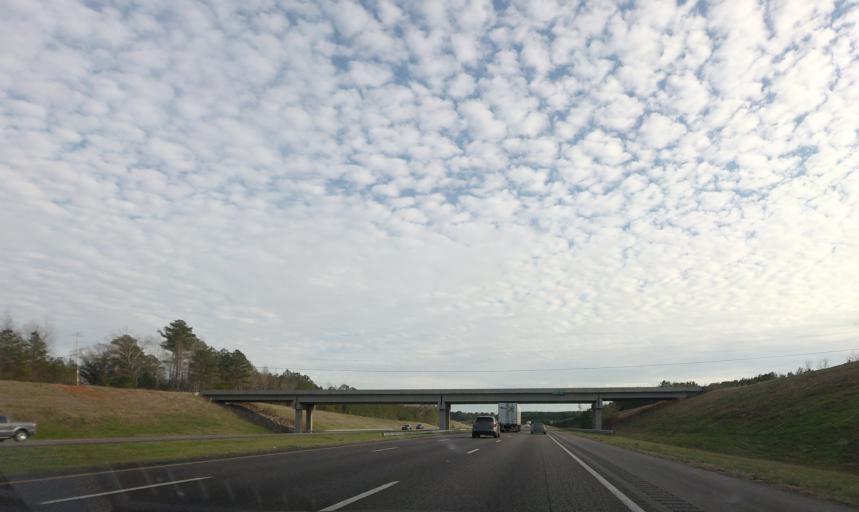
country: US
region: Alabama
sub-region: Walker County
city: Dora
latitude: 33.6713
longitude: -87.0750
